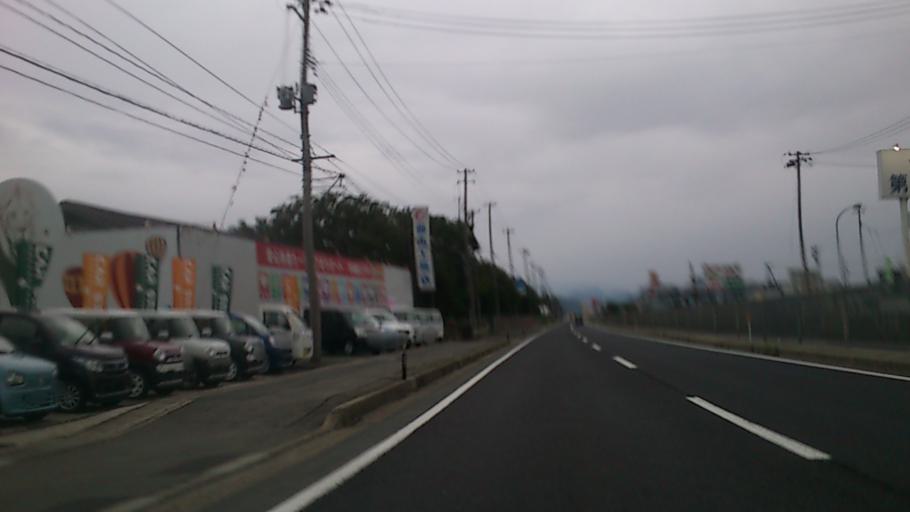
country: JP
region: Yamagata
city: Tendo
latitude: 38.3862
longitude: 140.3818
